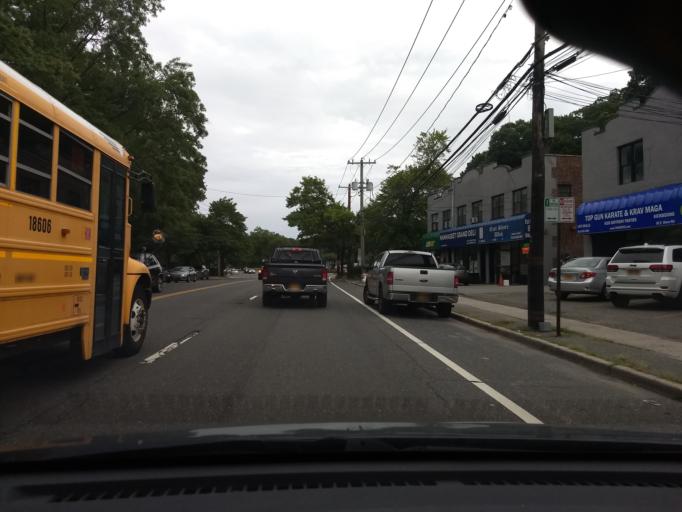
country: US
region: New York
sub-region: Nassau County
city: Thomaston
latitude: 40.7889
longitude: -73.7072
